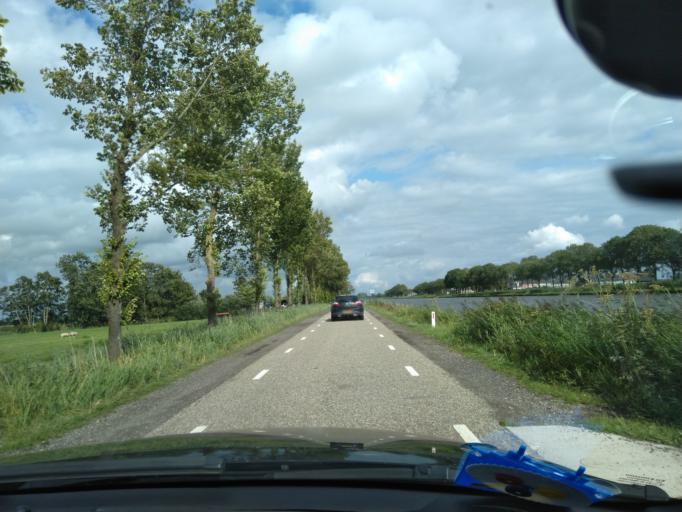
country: NL
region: Groningen
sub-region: Gemeente Zuidhorn
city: Grijpskerk
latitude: 53.2516
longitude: 6.3349
